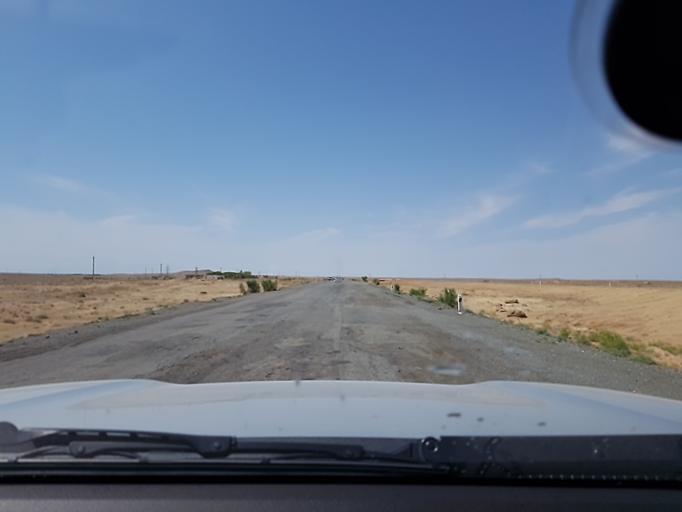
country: UZ
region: Karakalpakstan
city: Mang'it Shahri
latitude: 42.2641
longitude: 60.1187
